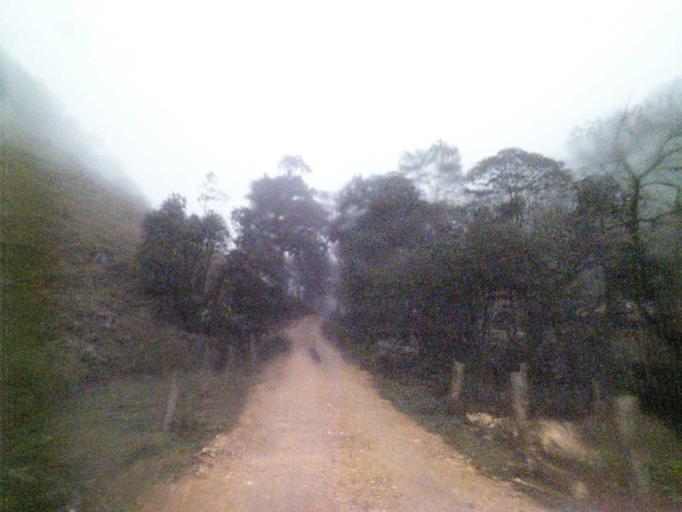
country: BR
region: Santa Catarina
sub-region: Anitapolis
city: Anitapolis
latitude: -27.7894
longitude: -49.1376
